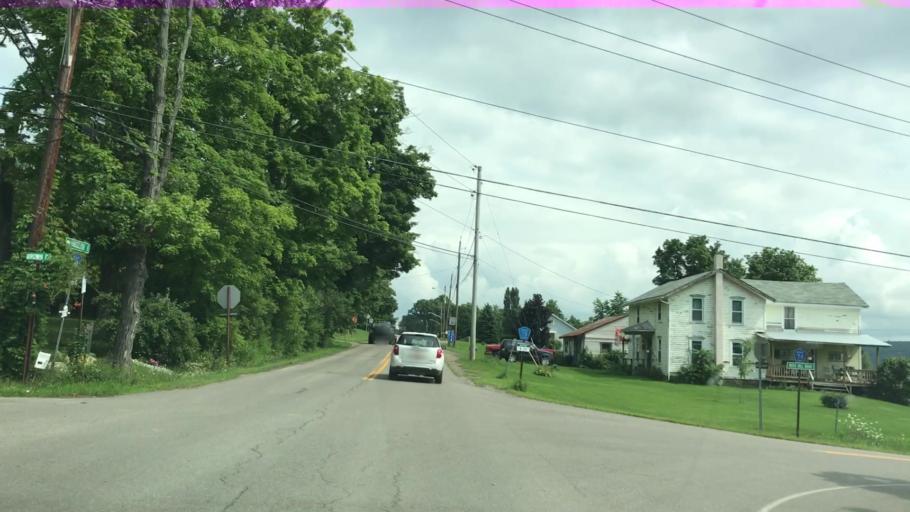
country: US
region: New York
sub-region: Steuben County
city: Sylvan Beach
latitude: 42.5282
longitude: -77.1651
